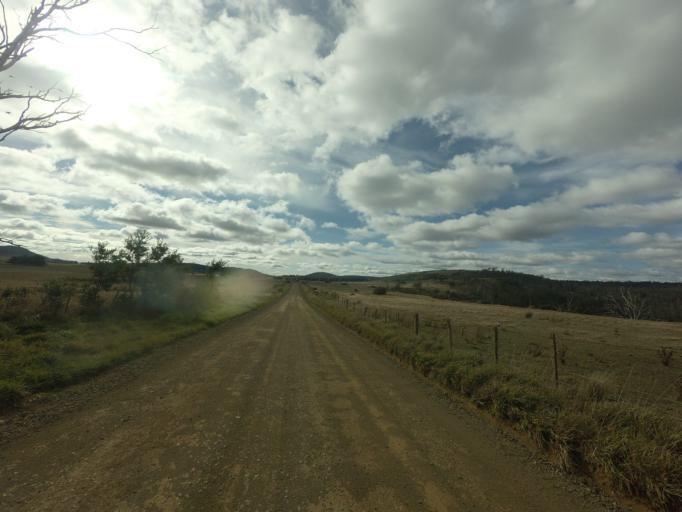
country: AU
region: Tasmania
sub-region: Brighton
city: Bridgewater
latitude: -42.4272
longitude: 147.3896
